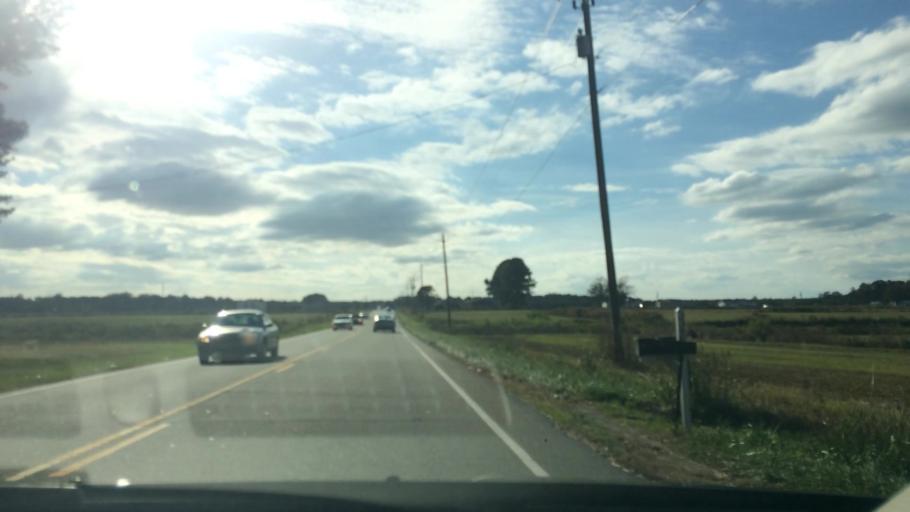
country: US
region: North Carolina
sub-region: Wayne County
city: Elroy
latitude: 35.4290
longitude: -77.8807
